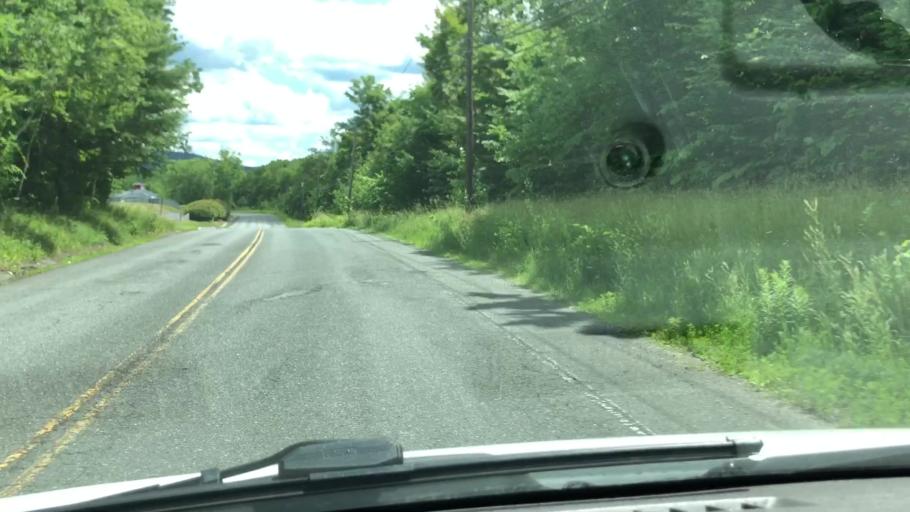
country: US
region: Massachusetts
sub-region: Berkshire County
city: Adams
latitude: 42.5935
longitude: -73.1170
